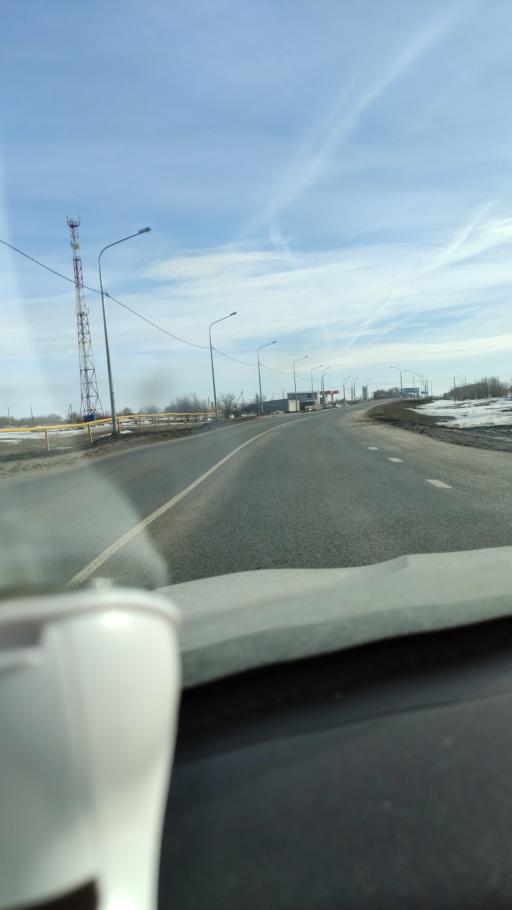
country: RU
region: Samara
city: Krasnoarmeyskoye
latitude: 52.8925
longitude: 49.9710
